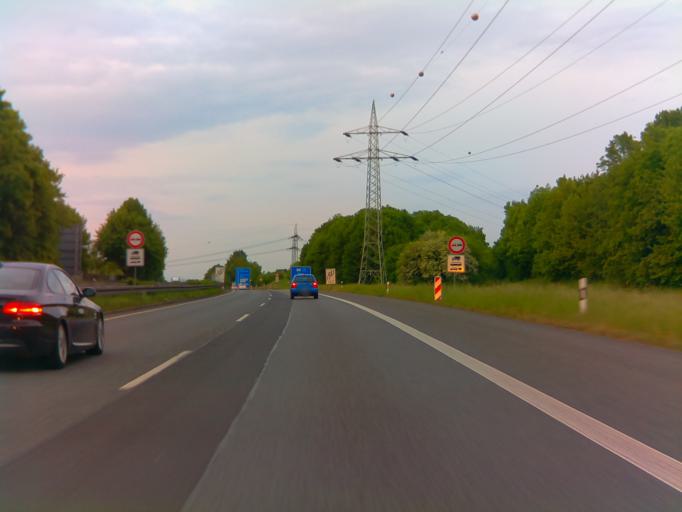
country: DE
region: Hesse
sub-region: Regierungsbezirk Kassel
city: Baunatal
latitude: 51.2483
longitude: 9.4379
